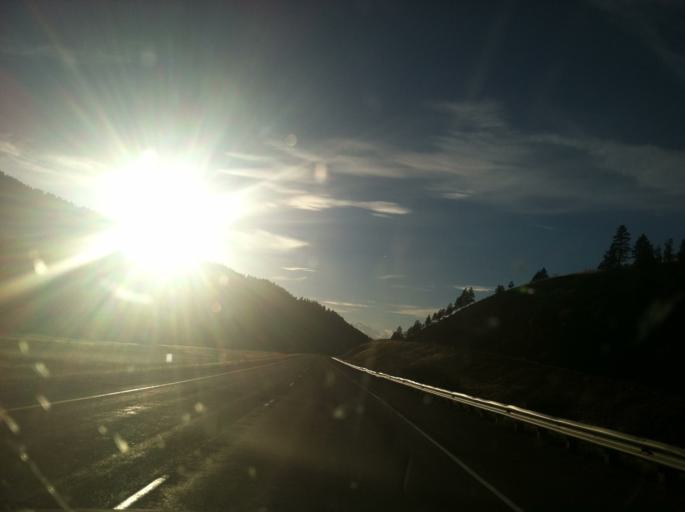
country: US
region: Montana
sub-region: Missoula County
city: Clinton
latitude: 46.7123
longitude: -113.5150
